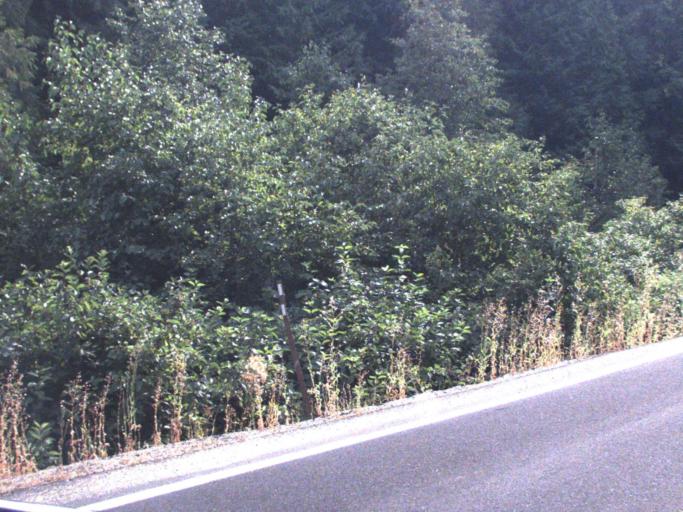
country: US
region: Washington
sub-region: Spokane County
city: Otis Orchards-East Farms
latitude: 47.8791
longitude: -117.1404
